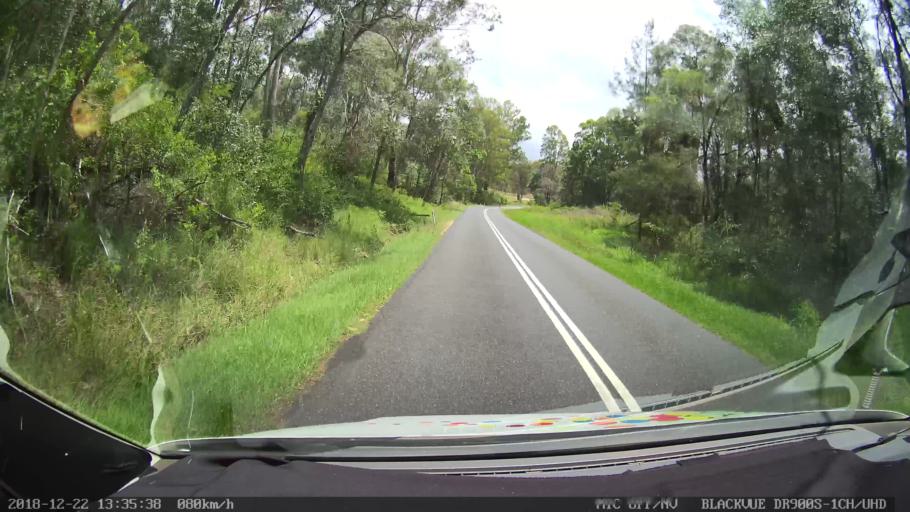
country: AU
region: New South Wales
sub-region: Clarence Valley
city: Coutts Crossing
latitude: -29.8741
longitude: 152.8033
